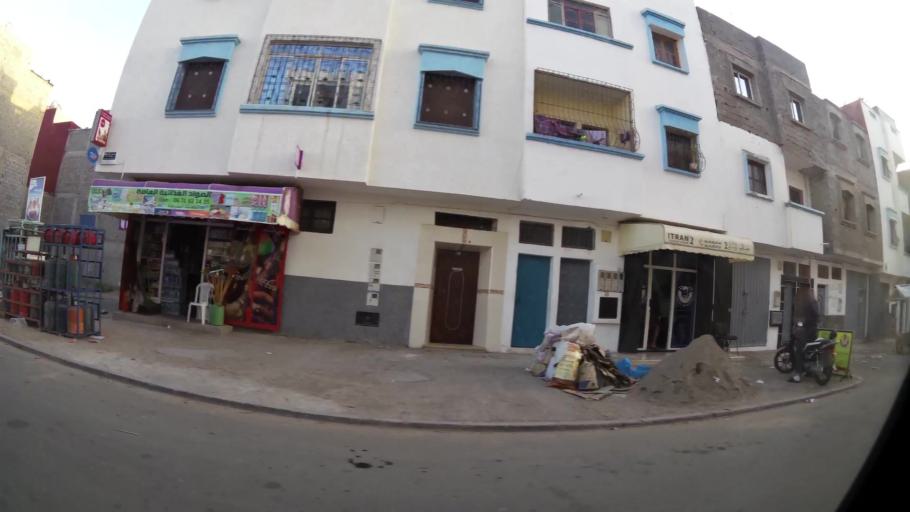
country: MA
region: Oued ed Dahab-Lagouira
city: Dakhla
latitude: 30.3976
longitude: -9.5589
